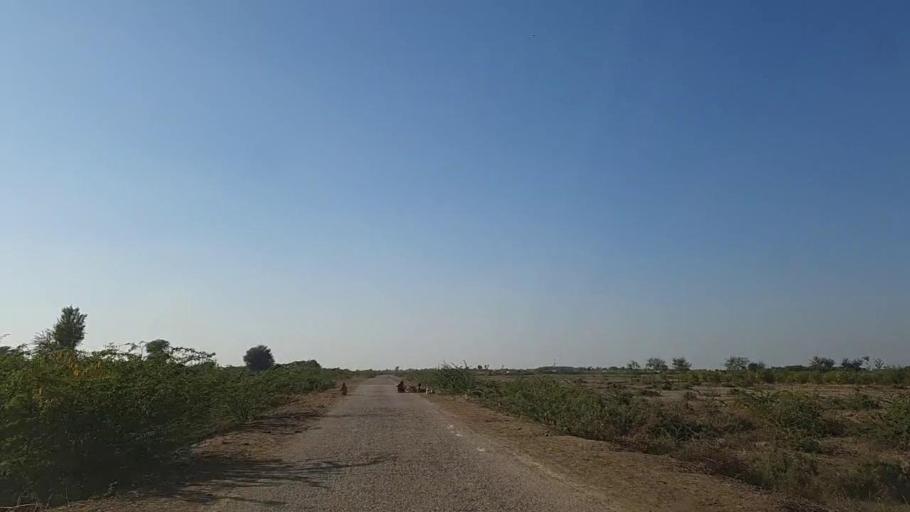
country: PK
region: Sindh
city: Samaro
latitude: 25.3537
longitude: 69.3814
